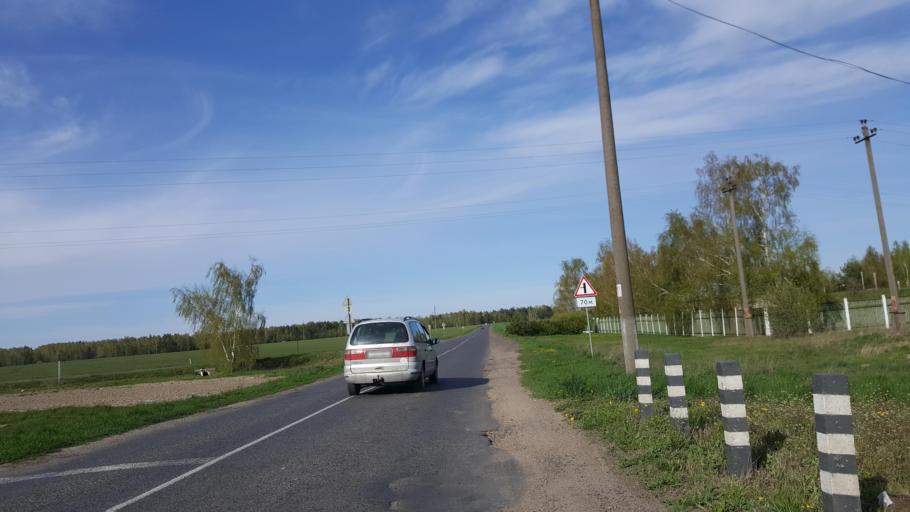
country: BY
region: Brest
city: Vysokaye
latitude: 52.3940
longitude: 23.4684
